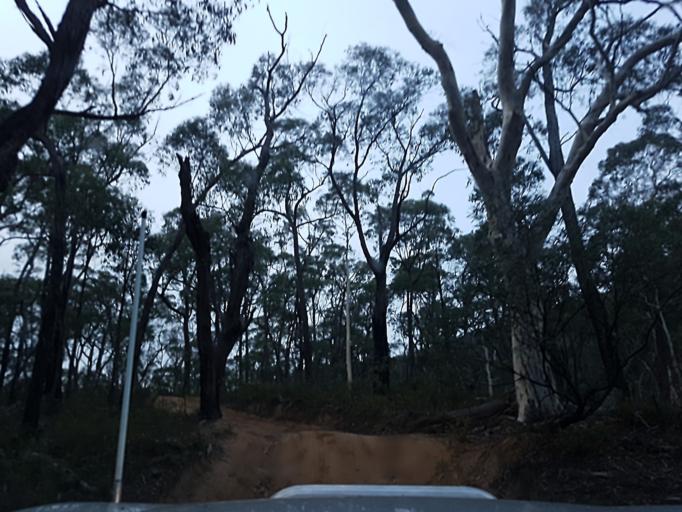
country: AU
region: New South Wales
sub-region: Snowy River
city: Jindabyne
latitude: -36.8641
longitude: 148.2369
